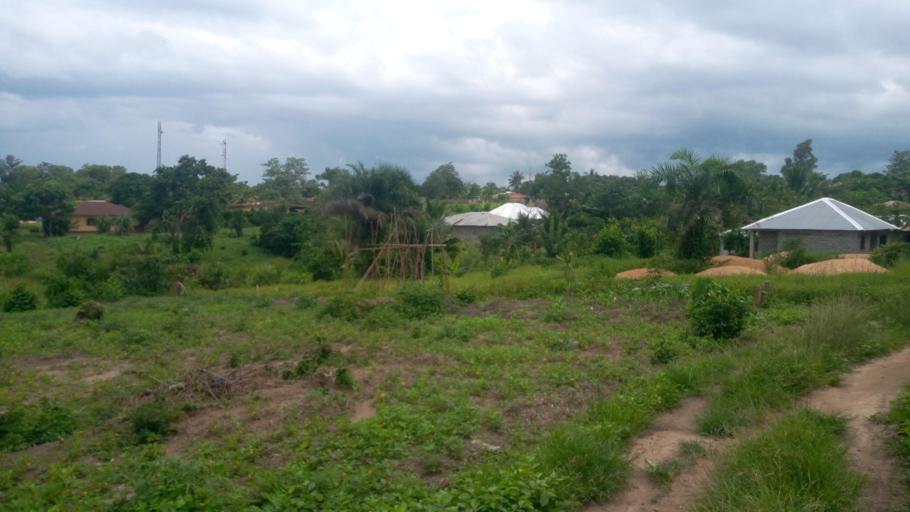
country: SL
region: Southern Province
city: Mogbwemo
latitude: 7.5991
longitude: -12.1696
